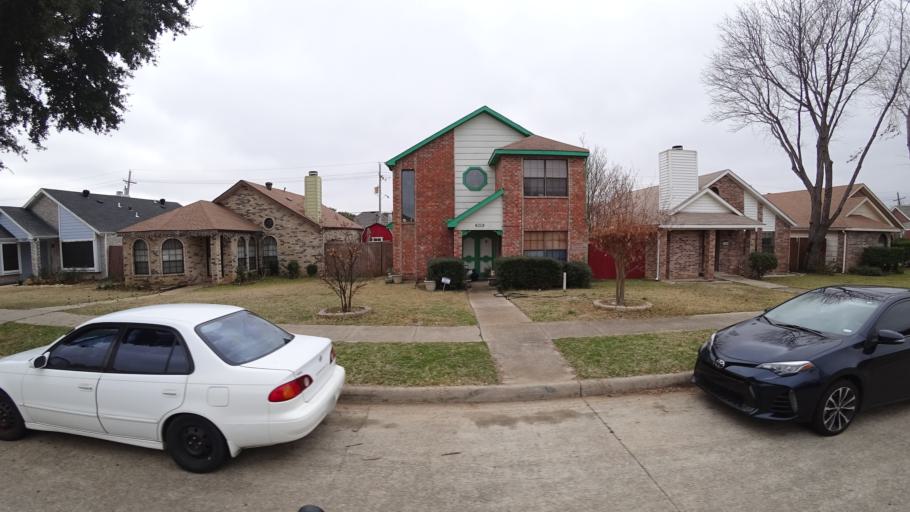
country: US
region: Texas
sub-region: Denton County
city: Lewisville
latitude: 33.0212
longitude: -97.0311
